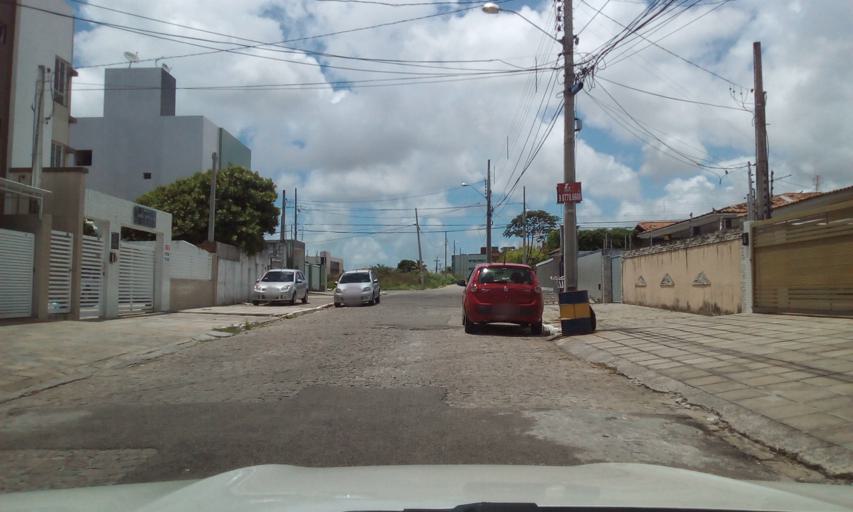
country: BR
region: Paraiba
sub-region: Joao Pessoa
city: Joao Pessoa
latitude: -7.1491
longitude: -34.8319
